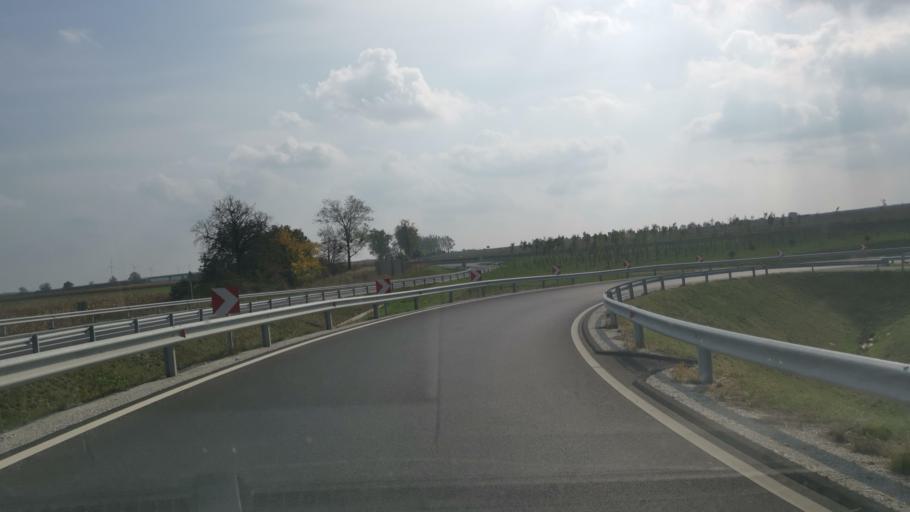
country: HU
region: Gyor-Moson-Sopron
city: Nagycenk
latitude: 47.5907
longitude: 16.7099
